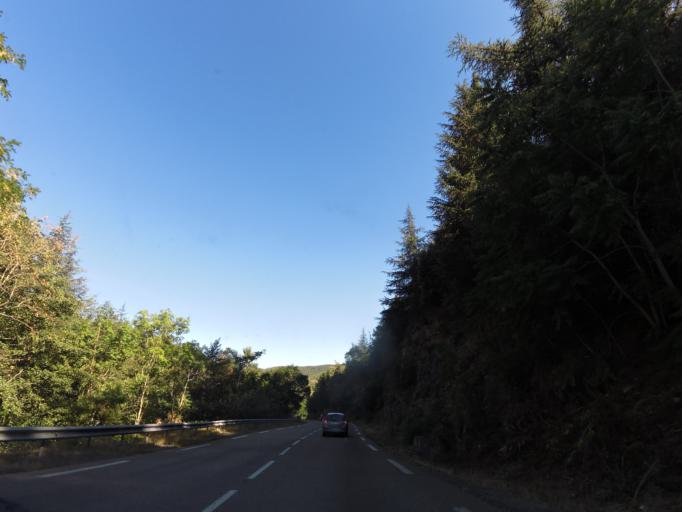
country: FR
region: Languedoc-Roussillon
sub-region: Departement du Gard
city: Valleraugue
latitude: 44.0537
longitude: 3.6872
